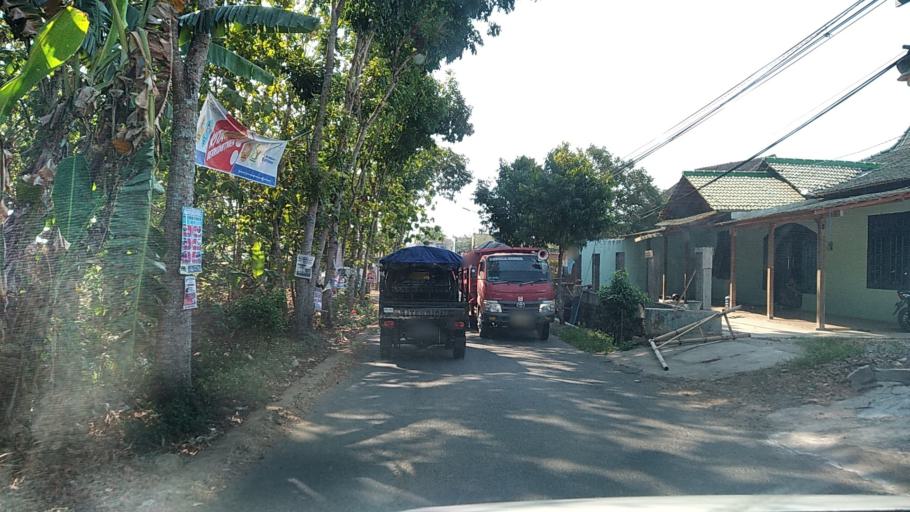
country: ID
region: Central Java
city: Ungaran
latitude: -7.0683
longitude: 110.3125
